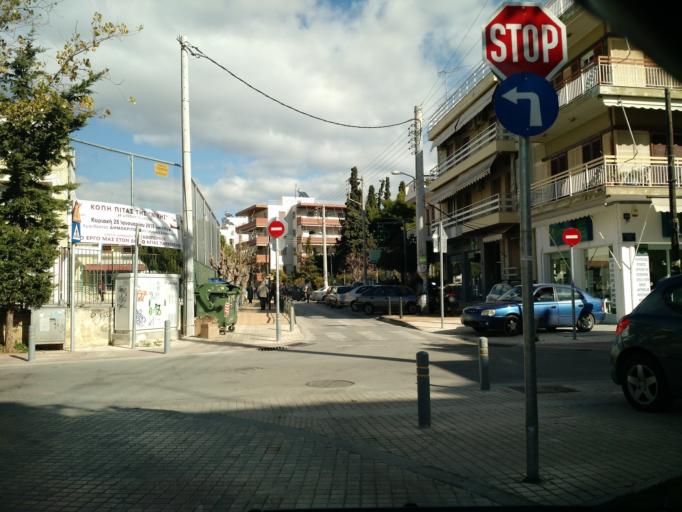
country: GR
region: Attica
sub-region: Nomarchia Athinas
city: Agia Paraskevi
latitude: 38.0188
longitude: 23.8256
